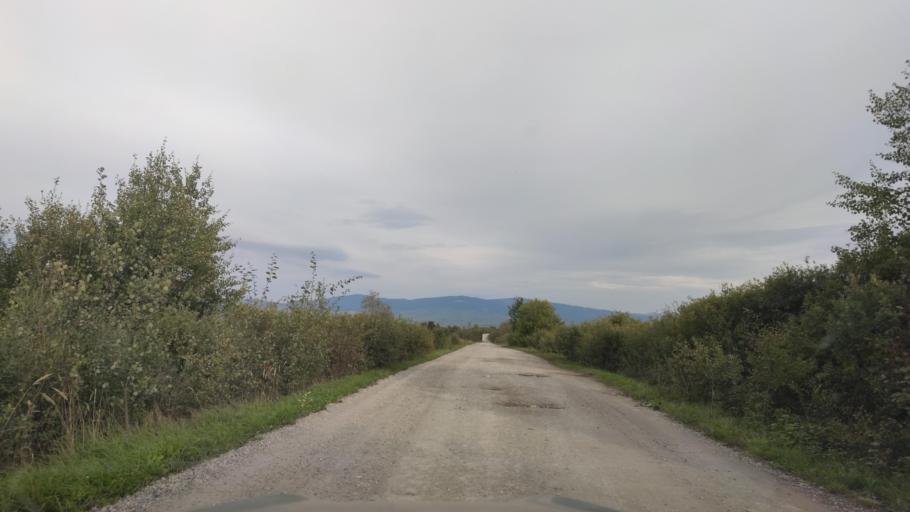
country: RO
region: Harghita
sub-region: Comuna Remetea
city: Remetea
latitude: 46.8119
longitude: 25.3796
